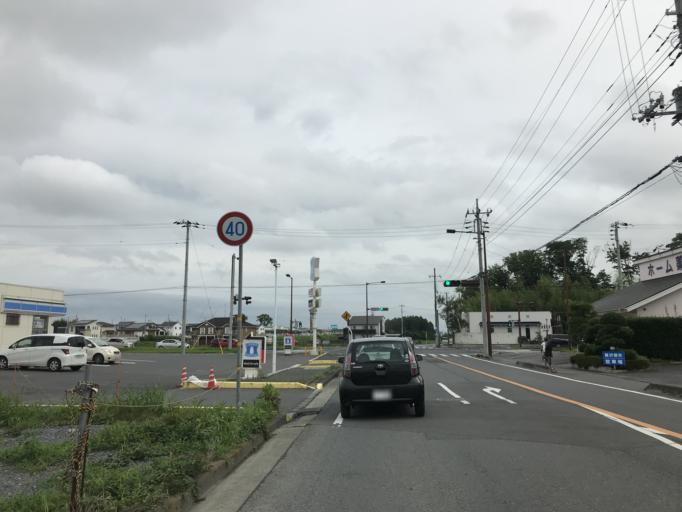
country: JP
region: Ibaraki
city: Mito-shi
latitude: 36.3363
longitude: 140.4589
